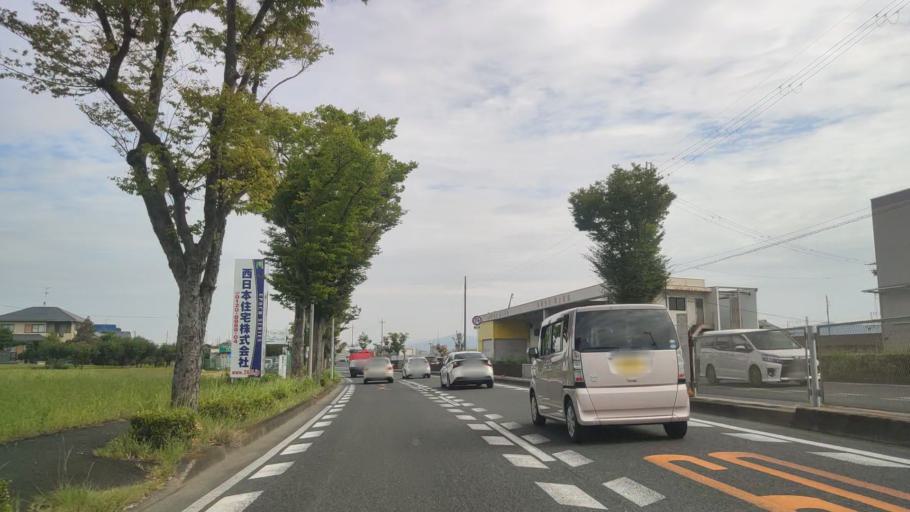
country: JP
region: Osaka
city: Tondabayashicho
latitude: 34.5144
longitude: 135.6046
